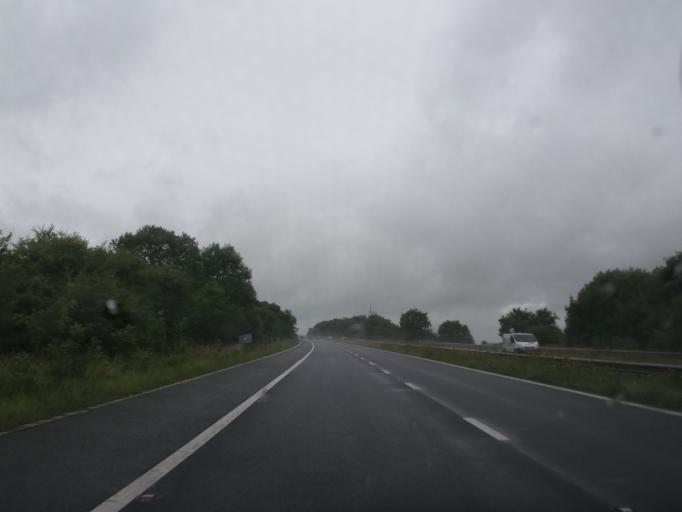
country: GB
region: England
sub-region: Rotherham
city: Bramley
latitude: 53.3954
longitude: -1.2702
